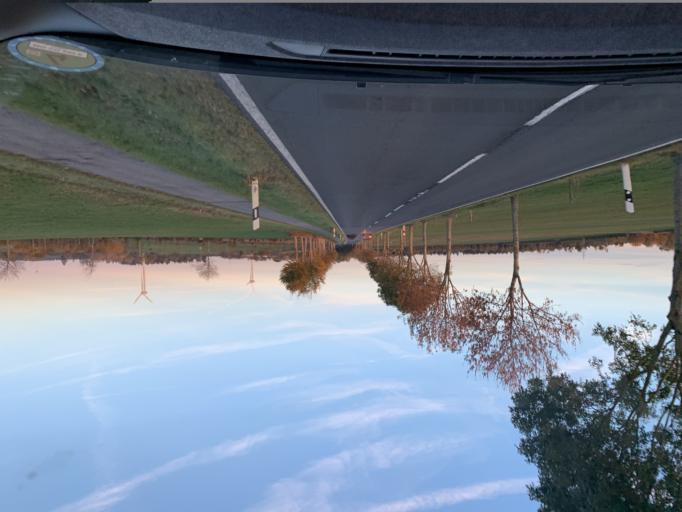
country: DE
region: North Rhine-Westphalia
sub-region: Regierungsbezirk Koln
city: Simmerath
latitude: 50.6373
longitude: 6.3439
